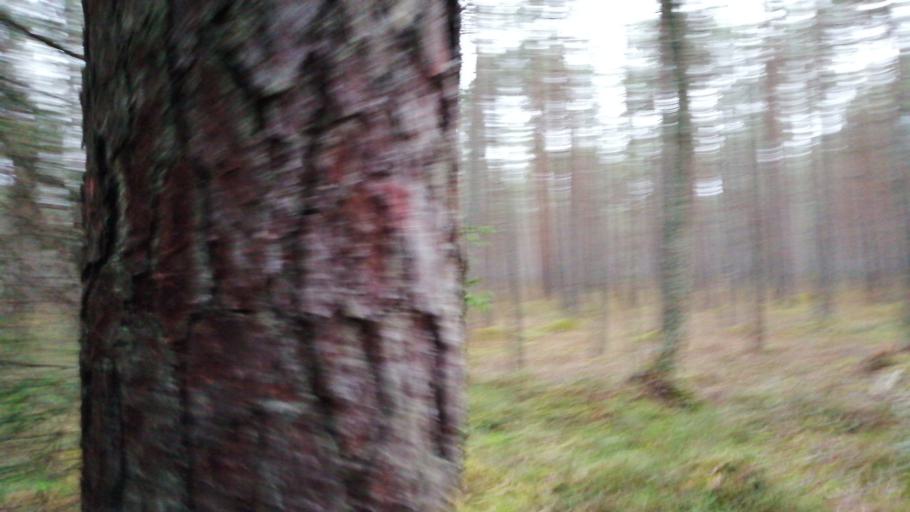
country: EE
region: Polvamaa
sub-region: Polva linn
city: Polva
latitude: 58.1543
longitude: 27.0651
